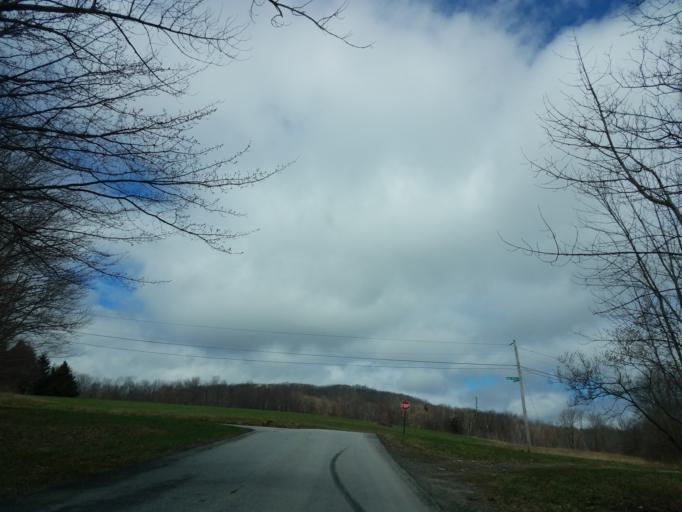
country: US
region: Connecticut
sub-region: Litchfield County
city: West Torrington
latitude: 41.7933
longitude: -73.1676
